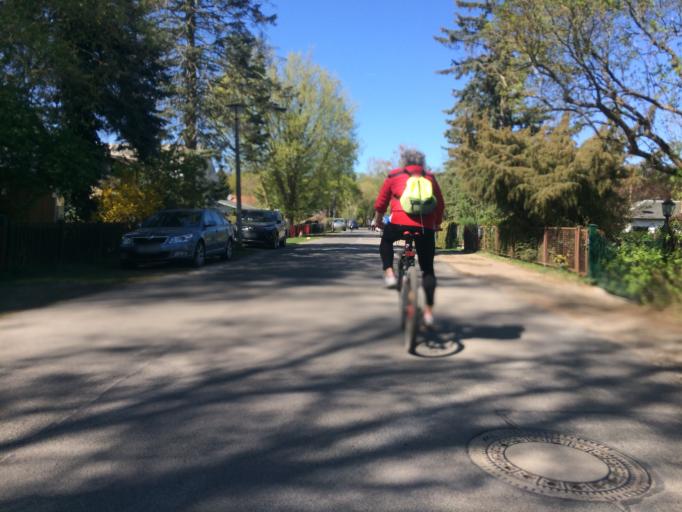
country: DE
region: Berlin
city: Rahnsdorf
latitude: 52.4373
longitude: 13.6863
